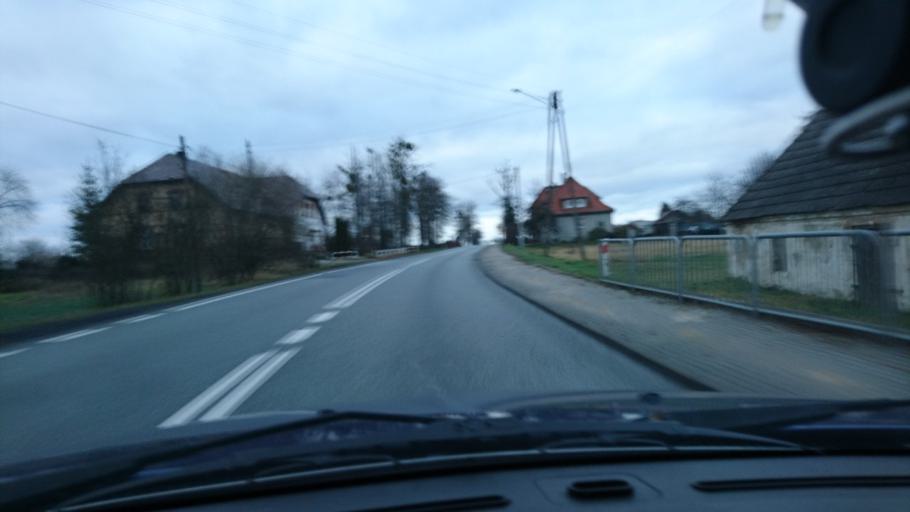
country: PL
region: Opole Voivodeship
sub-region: Powiat kluczborski
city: Byczyna
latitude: 51.0638
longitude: 18.2009
